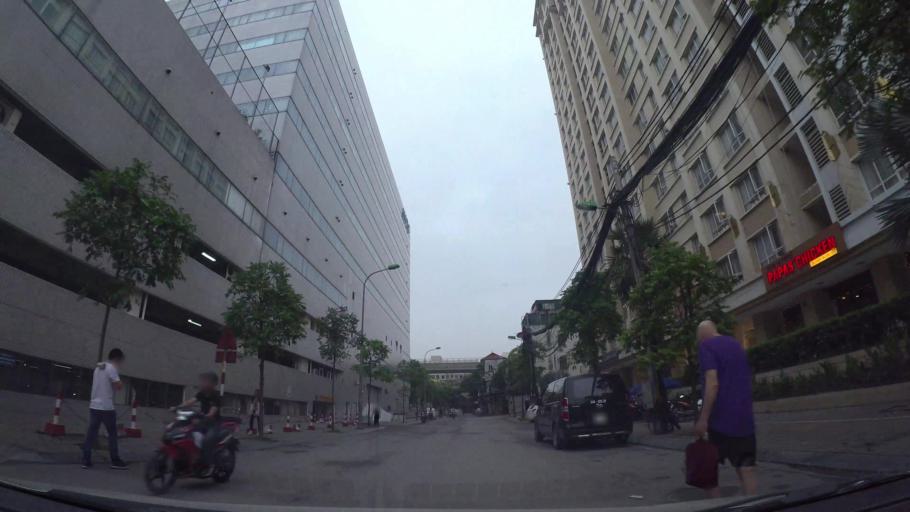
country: VN
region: Ha Noi
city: Cau Dien
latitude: 21.0356
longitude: 105.7836
